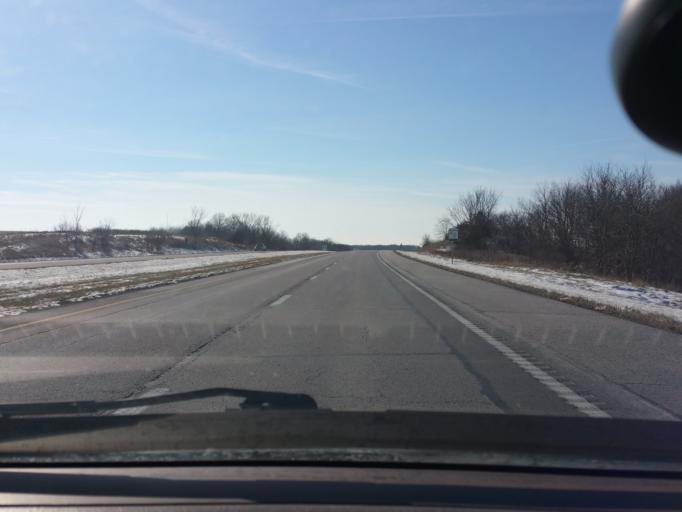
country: US
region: Missouri
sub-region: Harrison County
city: Bethany
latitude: 40.1123
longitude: -94.0648
